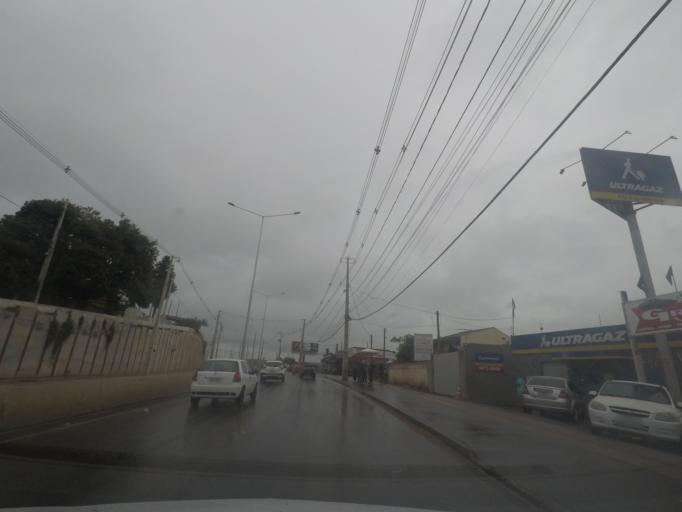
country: BR
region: Parana
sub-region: Piraquara
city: Piraquara
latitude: -25.4564
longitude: -49.0781
